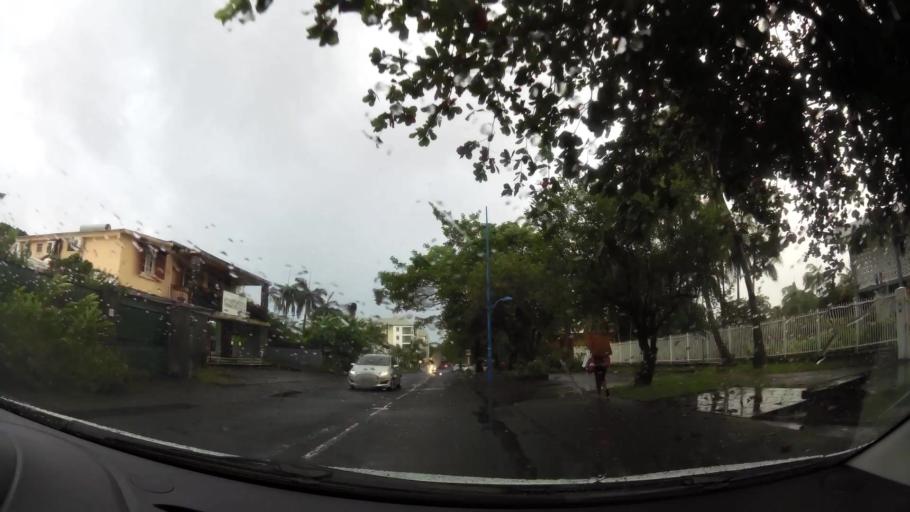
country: RE
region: Reunion
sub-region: Reunion
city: Saint-Benoit
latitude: -21.0373
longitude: 55.7117
